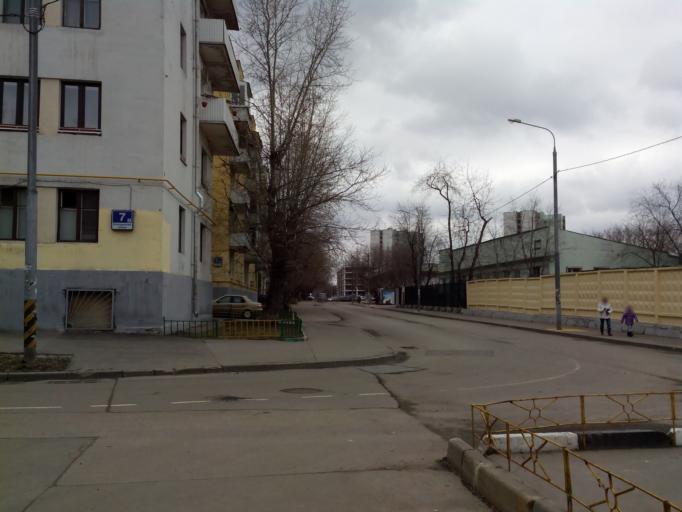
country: RU
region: Moskovskaya
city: Bogorodskoye
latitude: 55.7963
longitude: 37.6987
